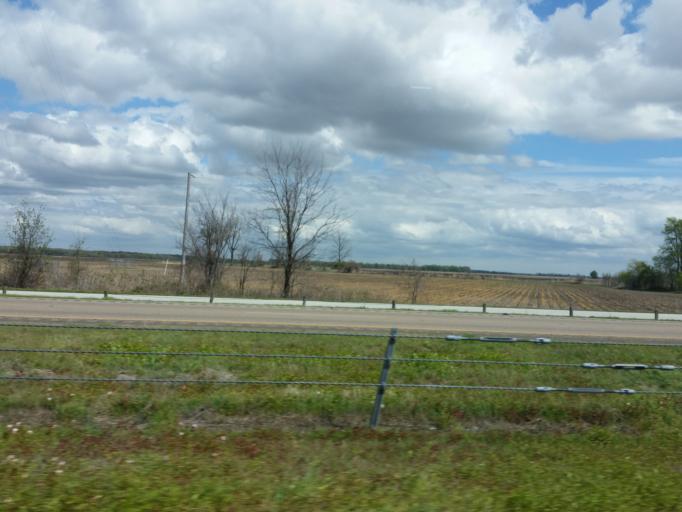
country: US
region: Arkansas
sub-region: Crittenden County
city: Marion
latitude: 35.3127
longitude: -90.2546
